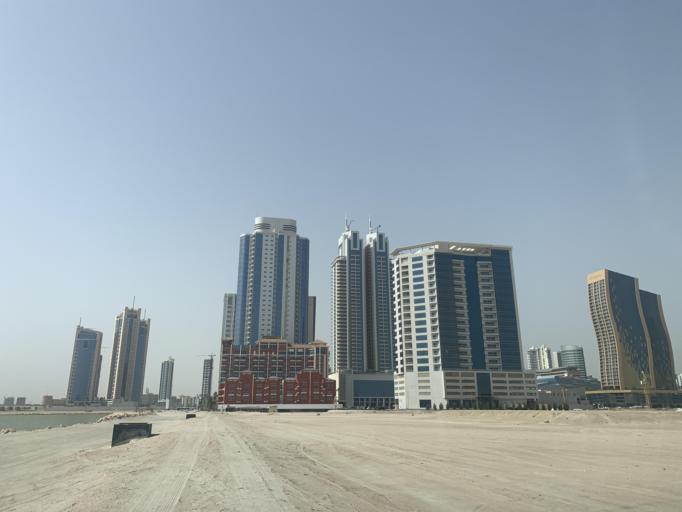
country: BH
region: Manama
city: Jidd Hafs
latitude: 26.2399
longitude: 50.5571
